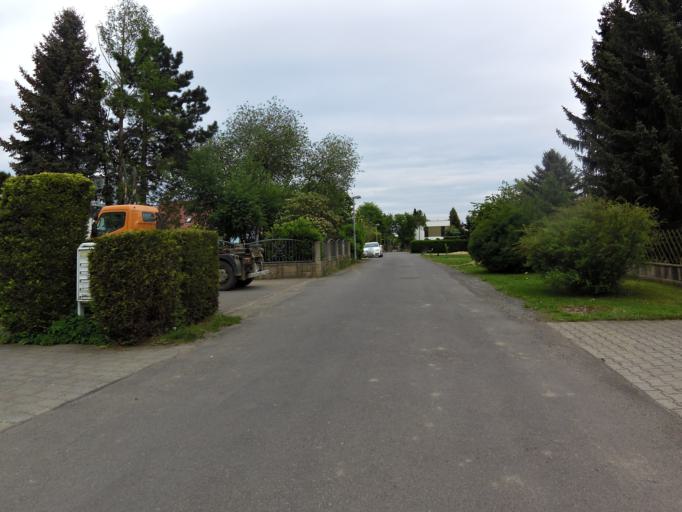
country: DE
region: Saxony
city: Markkleeberg
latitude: 51.2868
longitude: 12.2976
